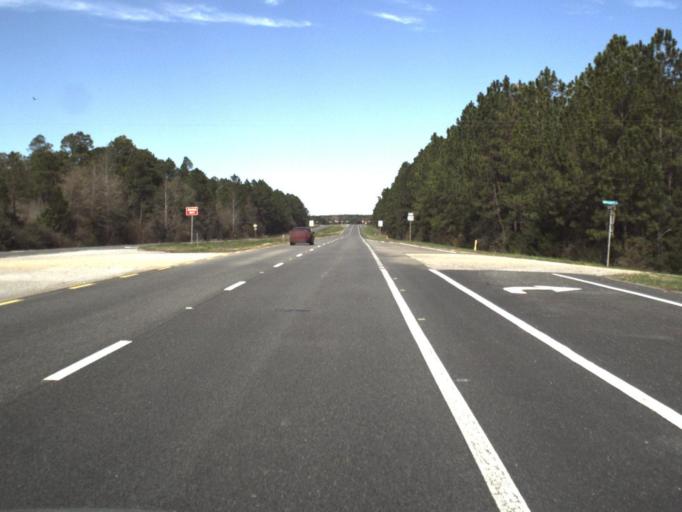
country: US
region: Florida
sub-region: Bay County
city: Youngstown
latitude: 30.5916
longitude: -85.3954
